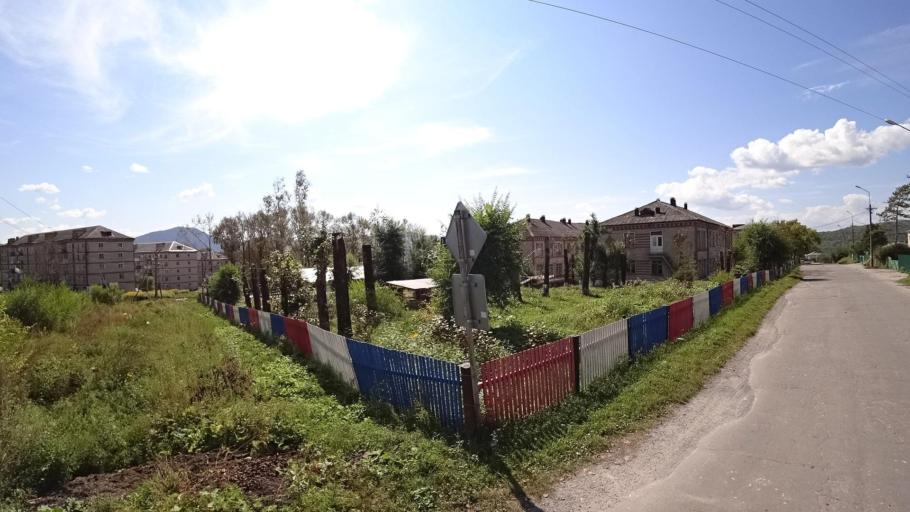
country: RU
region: Jewish Autonomous Oblast
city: Londoko
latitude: 49.0162
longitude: 131.8869
